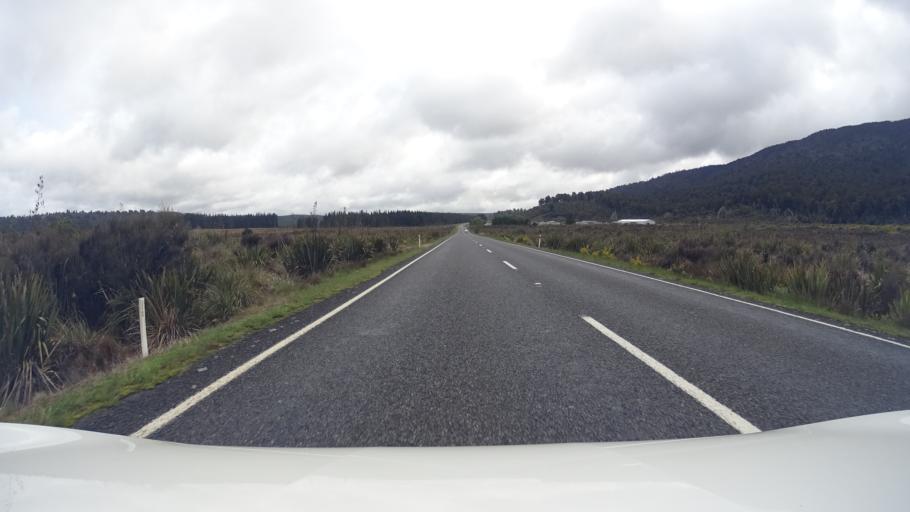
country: NZ
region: Manawatu-Wanganui
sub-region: Ruapehu District
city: Waiouru
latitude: -39.2314
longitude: 175.3941
